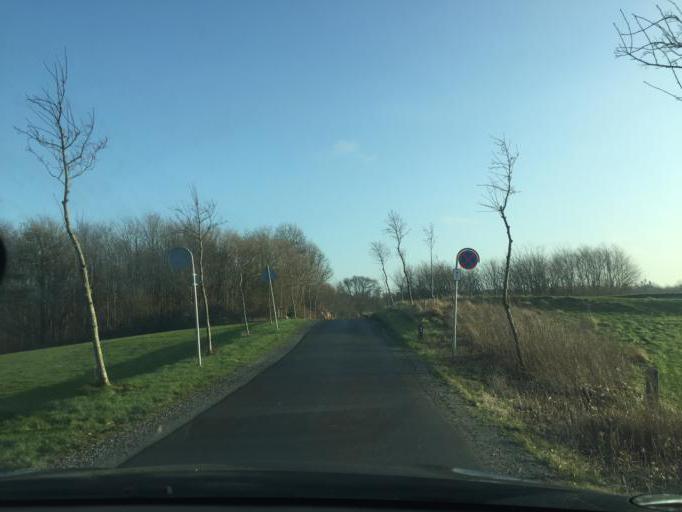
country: DK
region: South Denmark
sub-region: Faaborg-Midtfyn Kommune
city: Faaborg
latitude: 55.1369
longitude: 10.2508
